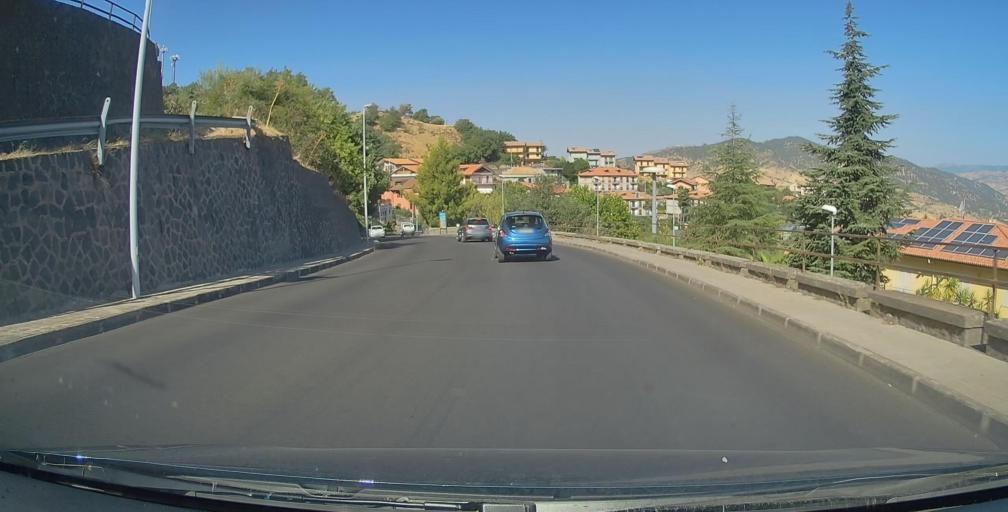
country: IT
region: Sicily
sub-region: Catania
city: Bronte
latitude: 37.7820
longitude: 14.8312
